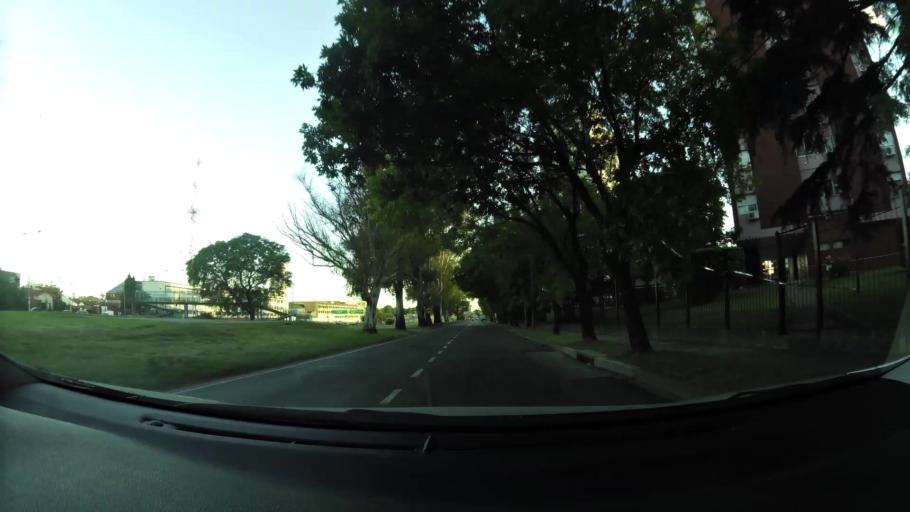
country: AR
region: Buenos Aires F.D.
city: Villa Lugano
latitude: -34.6958
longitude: -58.4743
